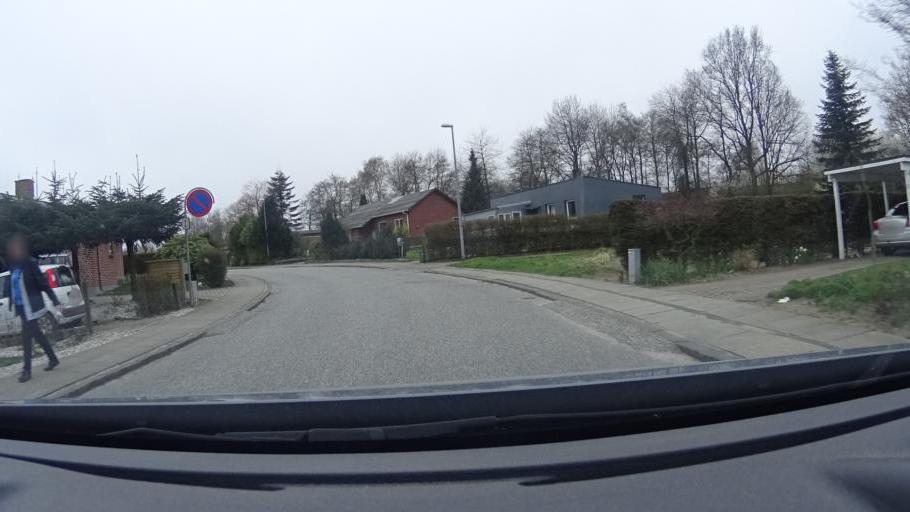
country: DK
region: South Denmark
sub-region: Vejle Kommune
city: Vejle
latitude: 55.7183
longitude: 9.5665
